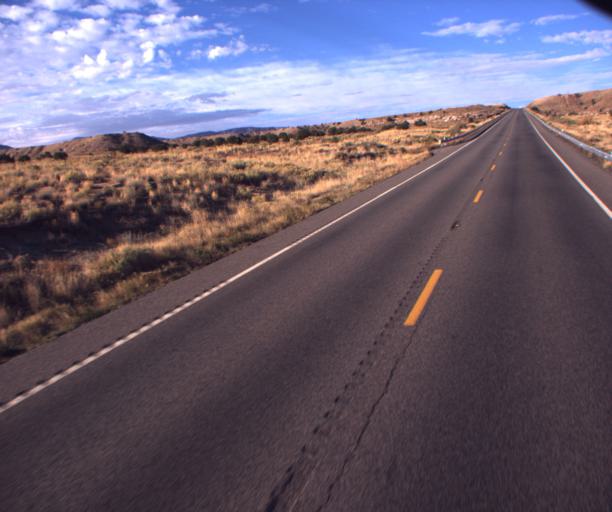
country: US
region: New Mexico
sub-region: San Juan County
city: Shiprock
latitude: 36.9307
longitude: -109.1513
